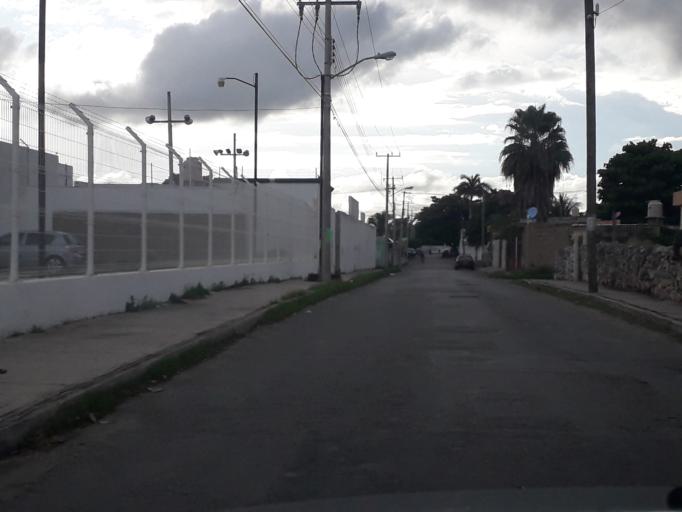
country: MX
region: Yucatan
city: Merida
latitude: 20.9607
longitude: -89.6608
